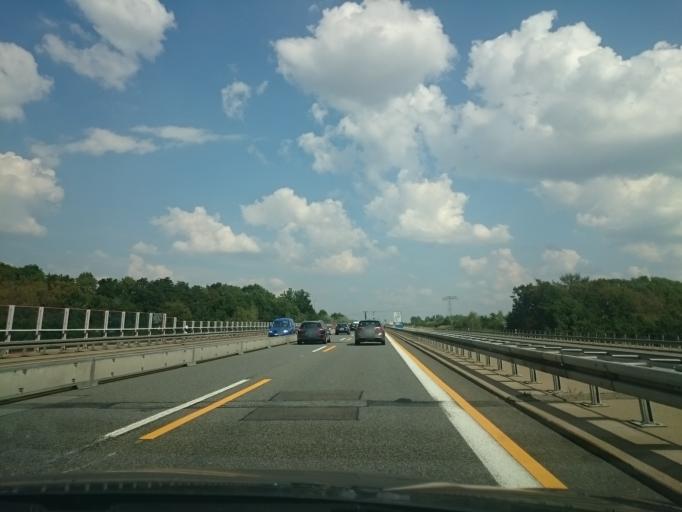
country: DE
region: Saxony
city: Hainichen
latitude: 50.9948
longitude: 13.1420
